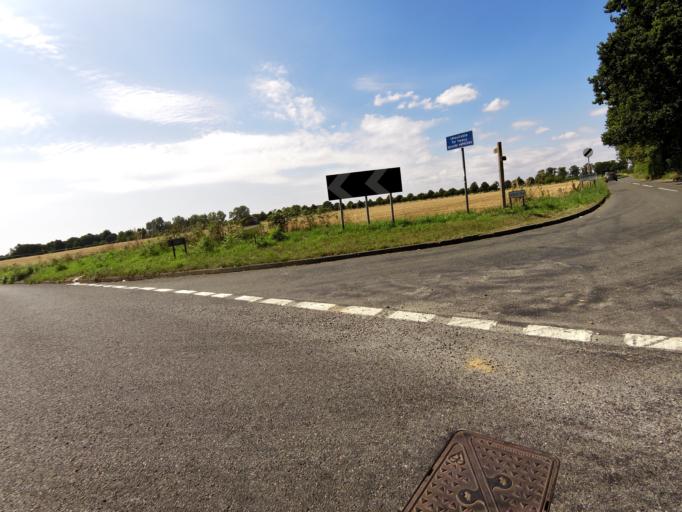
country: GB
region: England
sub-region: Suffolk
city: East Bergholt
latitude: 51.9600
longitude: 0.9649
